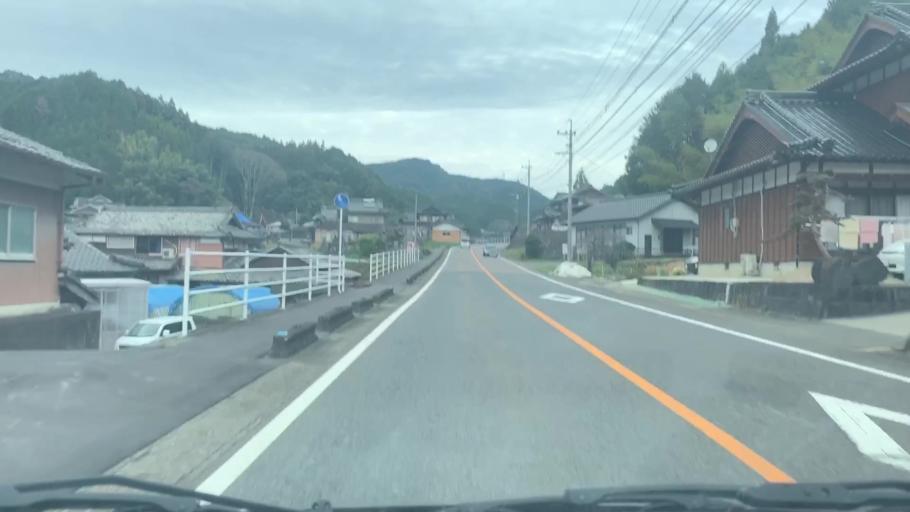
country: JP
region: Saga Prefecture
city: Ureshinomachi-shimojuku
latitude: 33.1523
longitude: 129.9736
